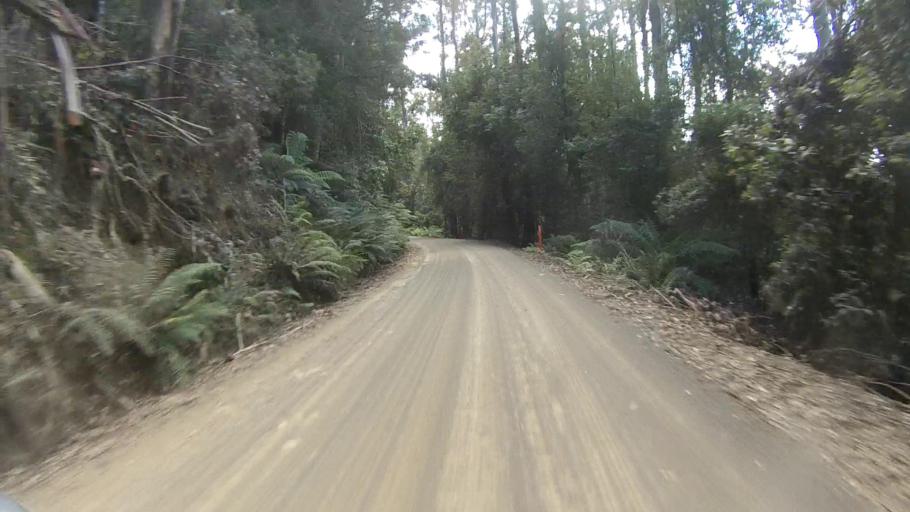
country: AU
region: Tasmania
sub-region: Derwent Valley
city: New Norfolk
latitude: -42.6804
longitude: 146.6872
